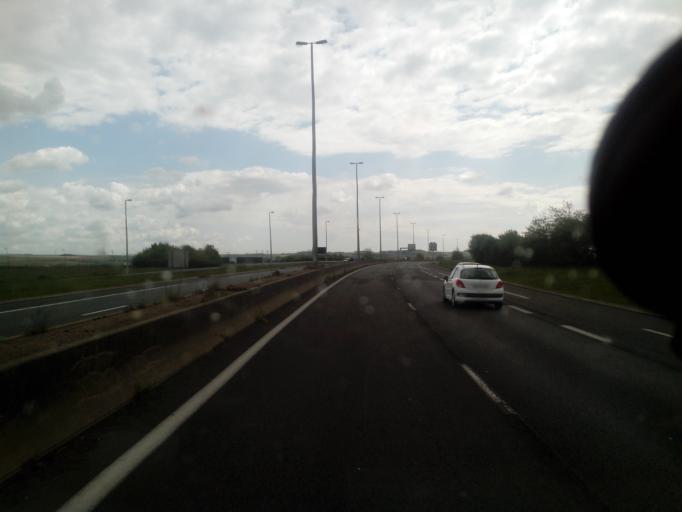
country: FR
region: Nord-Pas-de-Calais
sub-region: Departement du Pas-de-Calais
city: Coquelles
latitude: 50.9263
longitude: 1.8024
